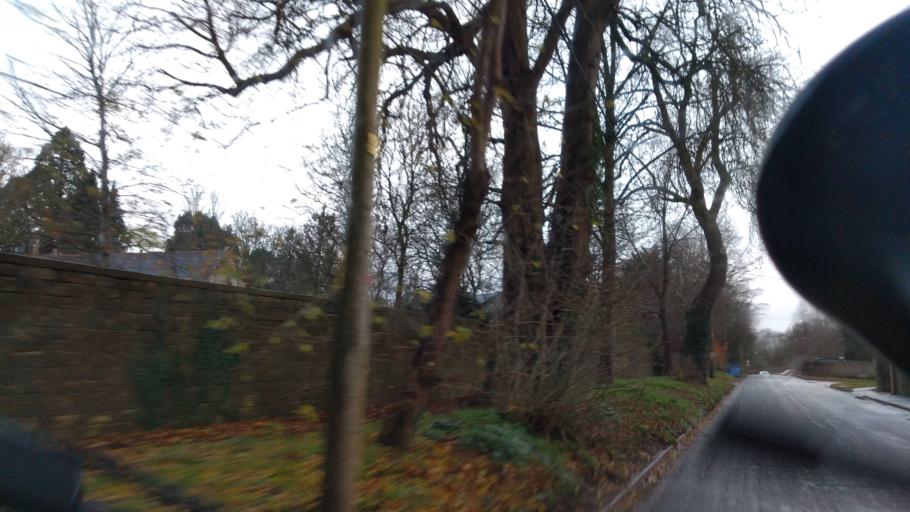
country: GB
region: England
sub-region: Wiltshire
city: Box
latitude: 51.4290
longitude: -2.2259
